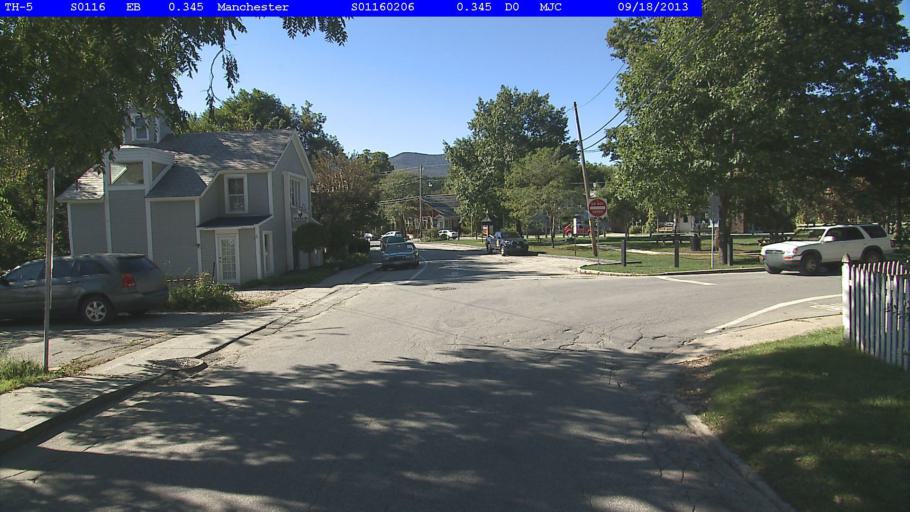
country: US
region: Vermont
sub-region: Bennington County
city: Manchester Center
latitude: 43.1772
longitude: -73.0526
